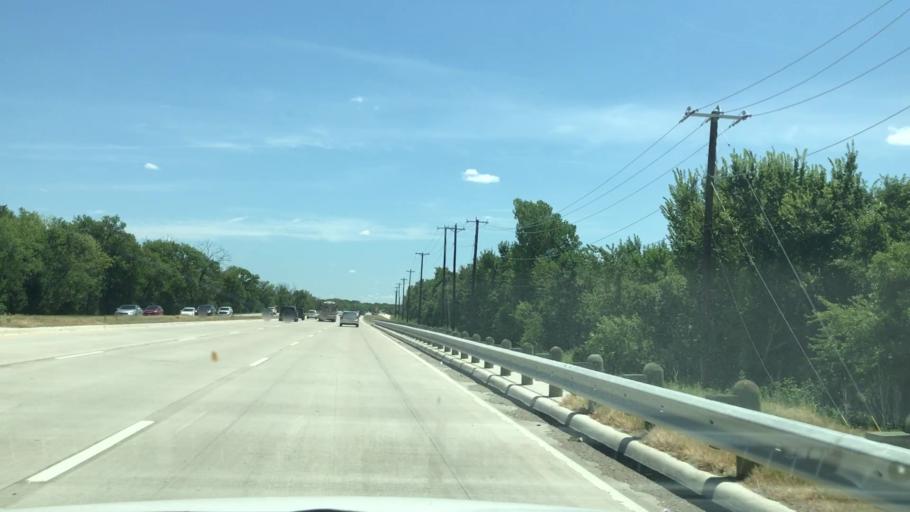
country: US
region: Texas
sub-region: Collin County
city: Lavon
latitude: 33.0252
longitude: -96.4824
